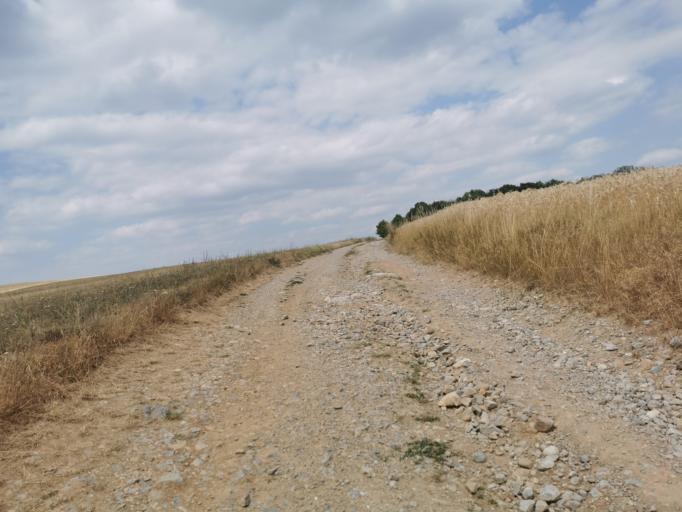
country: SK
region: Nitriansky
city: Brezova pod Bradlom
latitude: 48.6757
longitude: 17.4972
